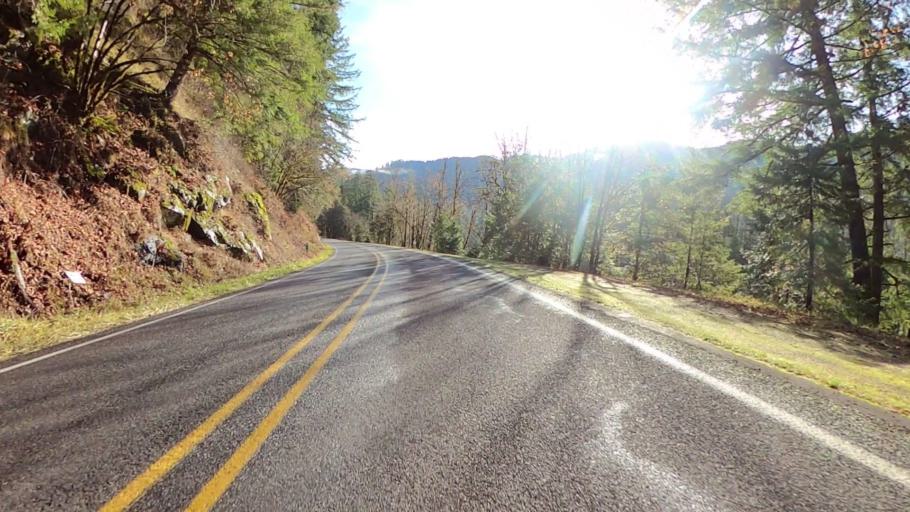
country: US
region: Oregon
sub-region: Lane County
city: Oakridge
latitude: 43.7508
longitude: -122.5258
